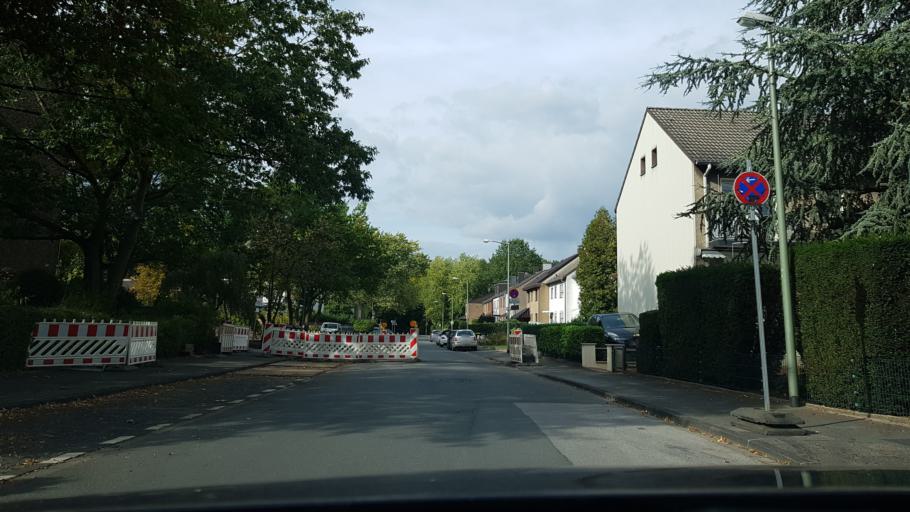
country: DE
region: North Rhine-Westphalia
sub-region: Regierungsbezirk Dusseldorf
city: Hochfeld
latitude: 51.3730
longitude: 6.7849
